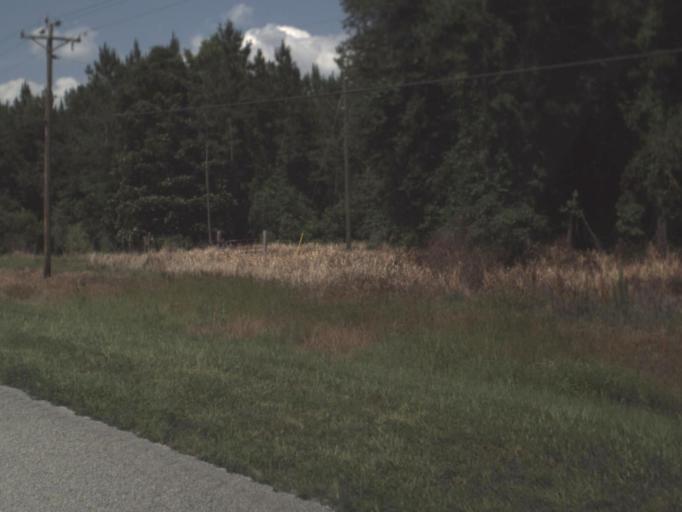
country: US
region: Florida
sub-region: Alachua County
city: Hawthorne
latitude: 29.5589
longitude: -82.0958
